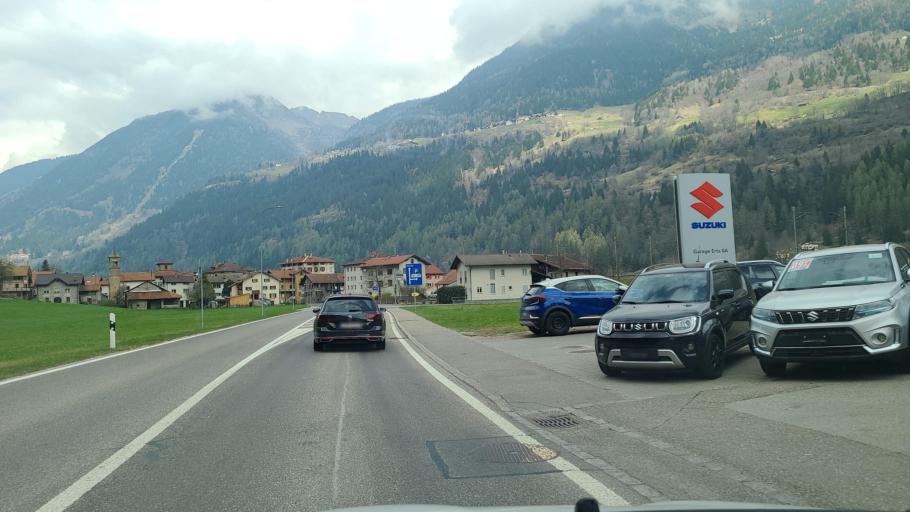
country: CH
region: Ticino
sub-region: Leventina District
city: Airolo
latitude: 46.5064
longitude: 8.7053
